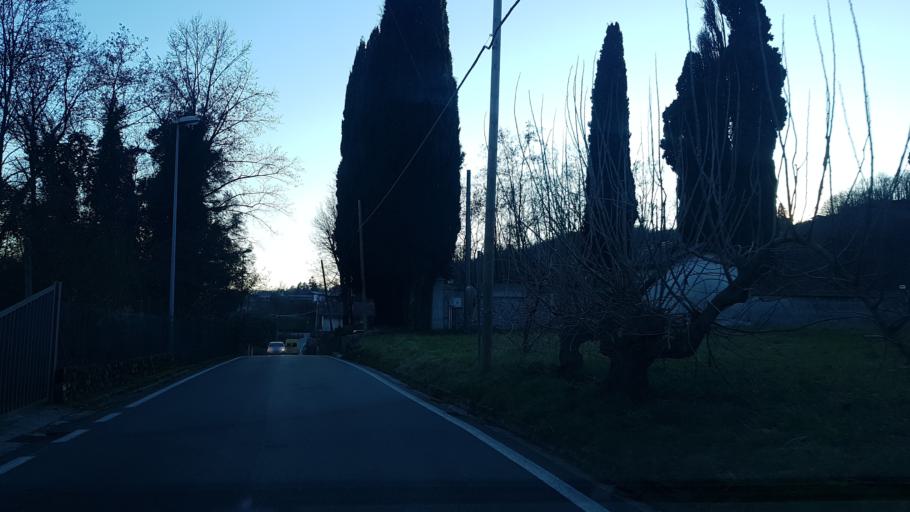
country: IT
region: Friuli Venezia Giulia
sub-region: Provincia di Udine
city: Tarcento
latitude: 46.2297
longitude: 13.2240
